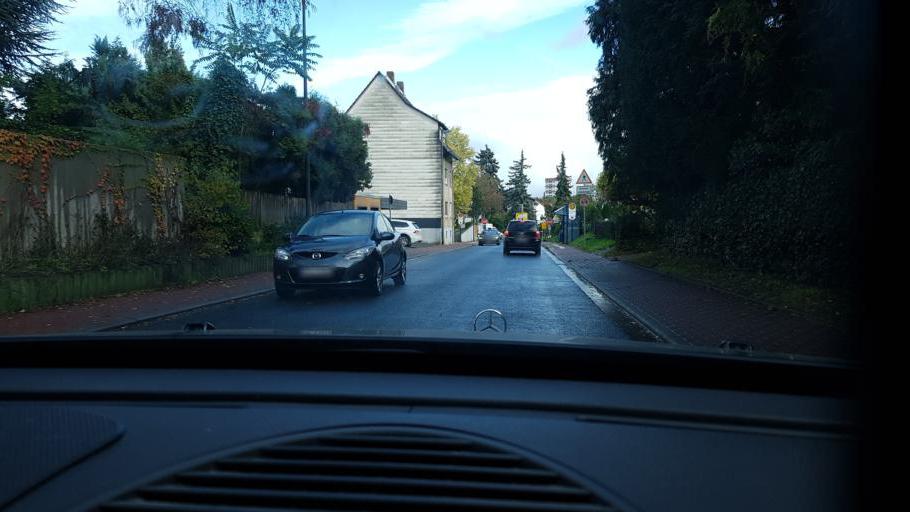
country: DE
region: Hesse
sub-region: Regierungsbezirk Darmstadt
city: Steinbach am Taunus
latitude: 50.1666
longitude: 8.5677
